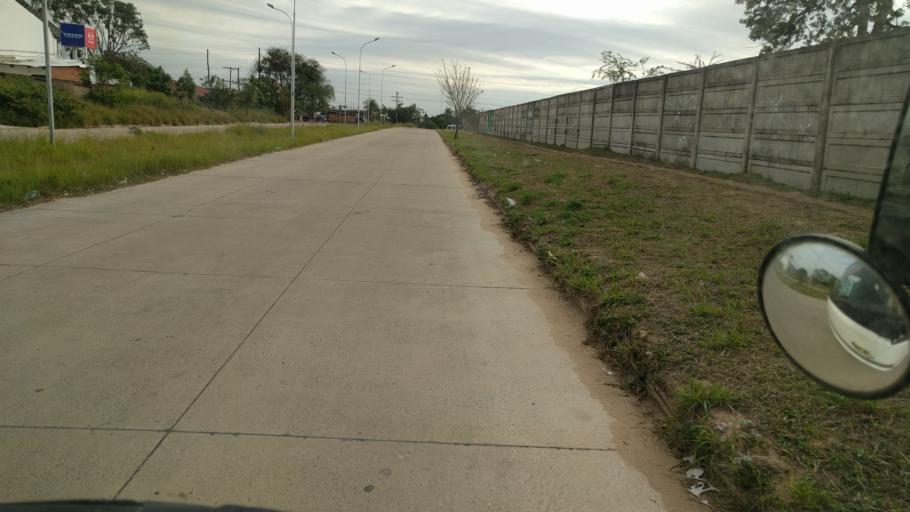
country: BO
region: Santa Cruz
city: Santa Cruz de la Sierra
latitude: -17.6833
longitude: -63.1574
